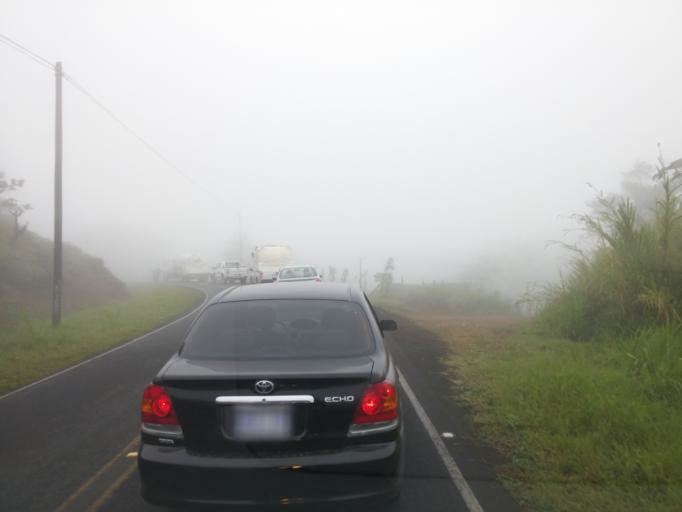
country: CR
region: Alajuela
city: San Ramon
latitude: 10.1794
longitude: -84.5018
